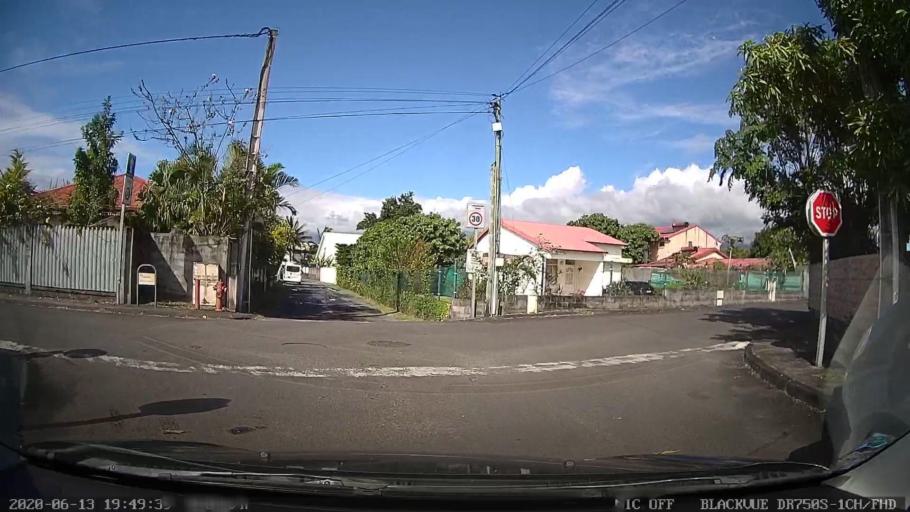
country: RE
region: Reunion
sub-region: Reunion
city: Bras-Panon
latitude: -21.0048
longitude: 55.6887
